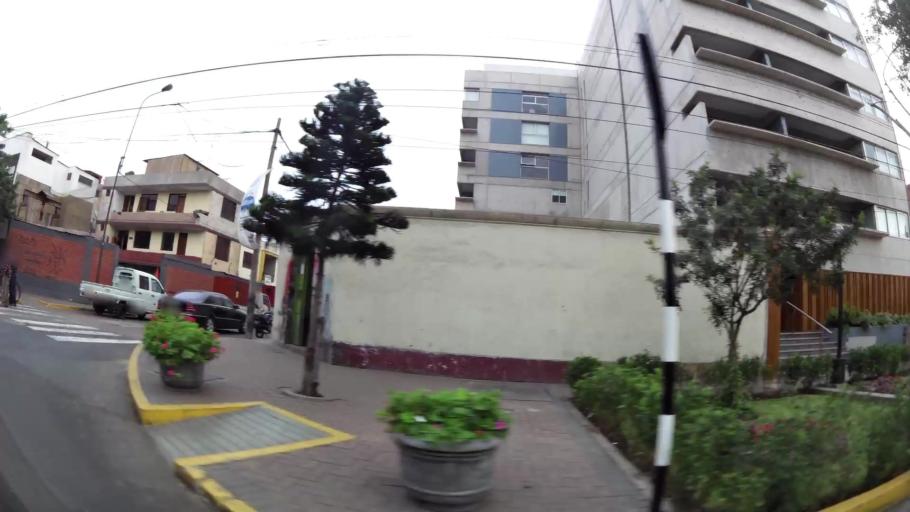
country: PE
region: Lima
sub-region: Lima
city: San Isidro
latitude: -12.1104
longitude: -77.0473
